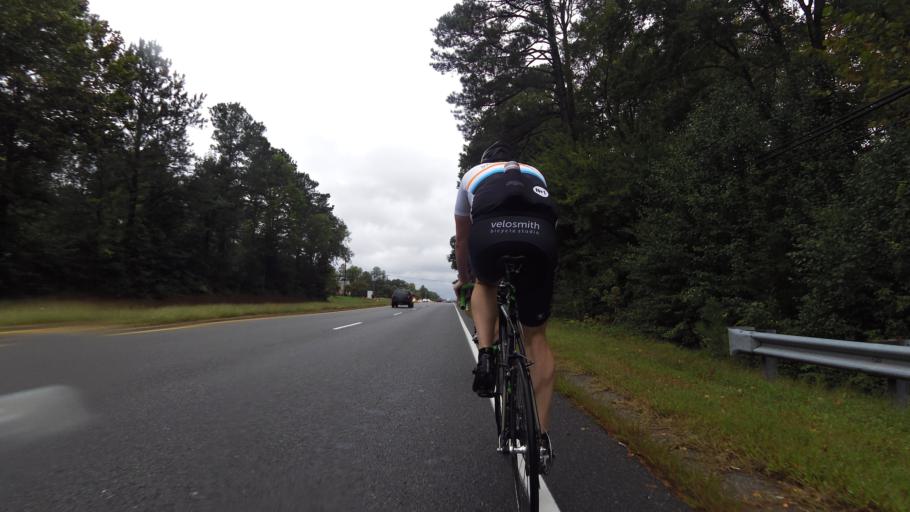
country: US
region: Virginia
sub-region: Henrico County
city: Tuckahoe
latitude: 37.5967
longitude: -77.6015
